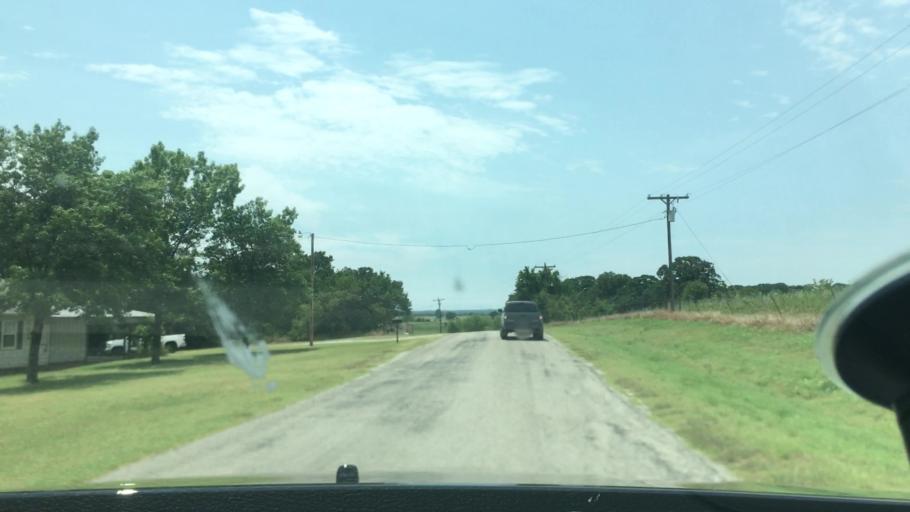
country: US
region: Texas
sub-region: Cooke County
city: Muenster
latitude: 33.8848
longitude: -97.3559
